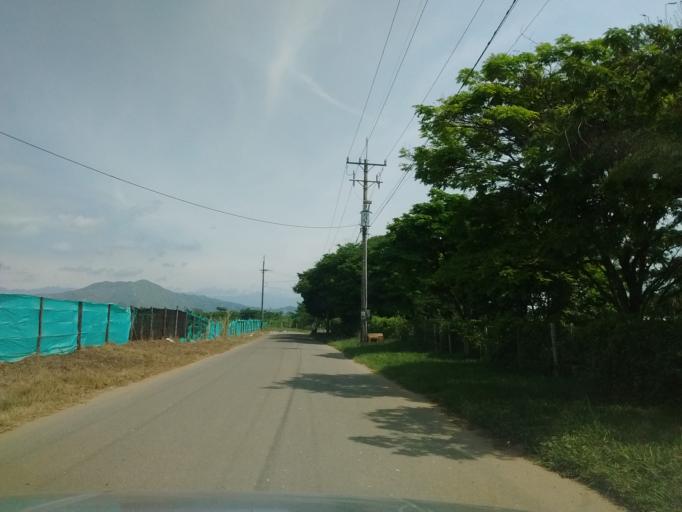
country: CO
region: Cauca
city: Santander de Quilichao
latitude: 3.0250
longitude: -76.4862
